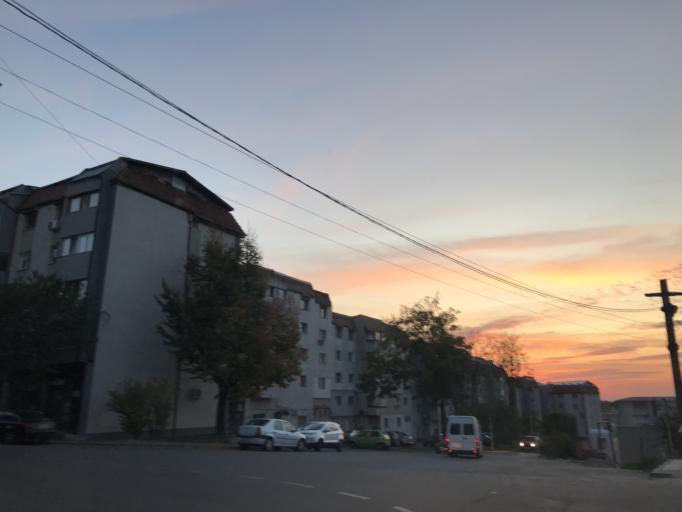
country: RO
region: Olt
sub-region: Municipiul Slatina
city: Slatina
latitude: 44.4315
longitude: 24.3612
